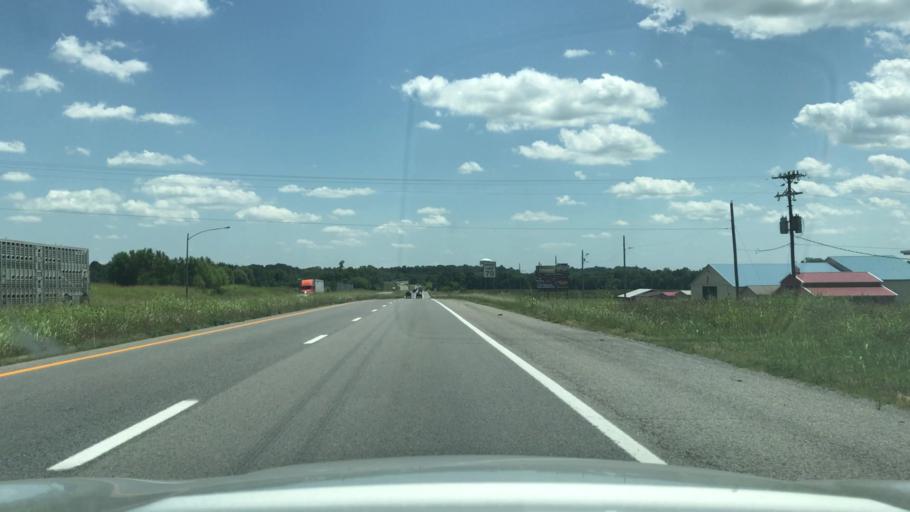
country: US
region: Kentucky
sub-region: Christian County
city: Hopkinsville
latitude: 36.8914
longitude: -87.4691
